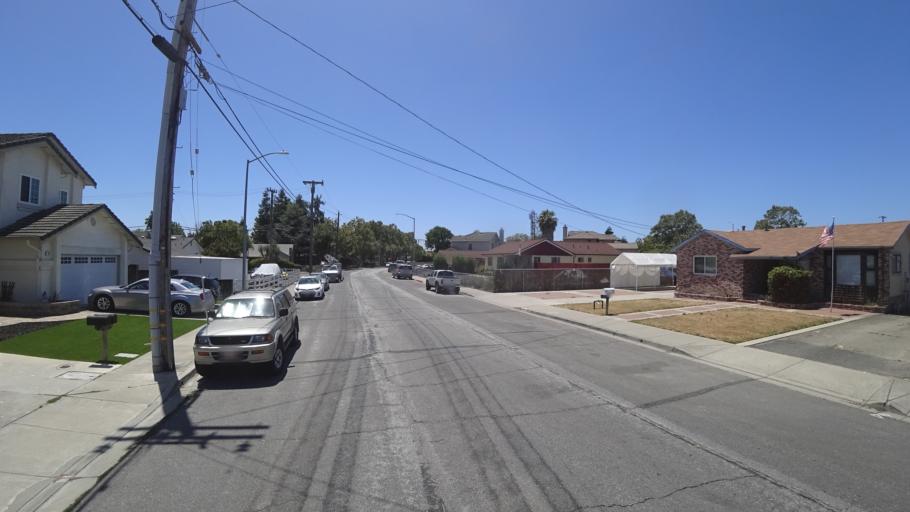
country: US
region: California
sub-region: Alameda County
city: Hayward
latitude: 37.6278
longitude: -122.0587
